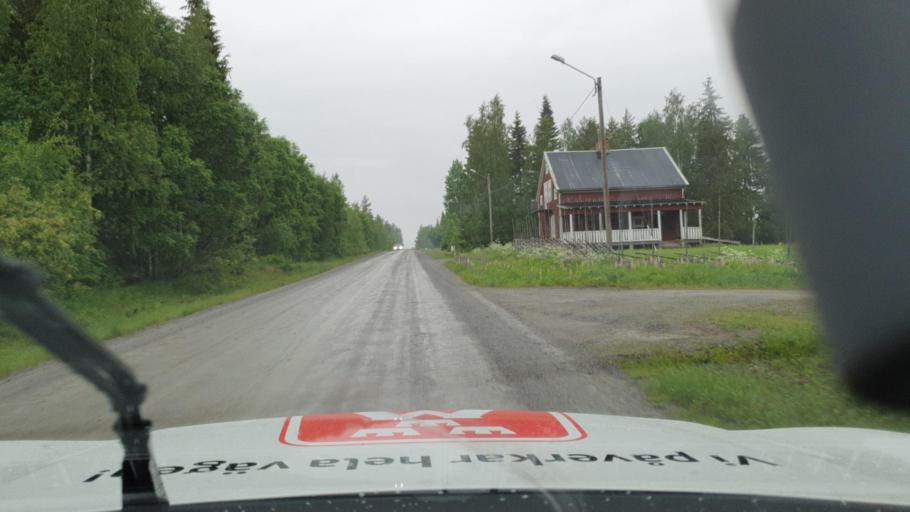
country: SE
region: Vaesterbotten
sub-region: Bjurholms Kommun
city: Bjurholm
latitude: 63.8570
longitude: 19.4710
